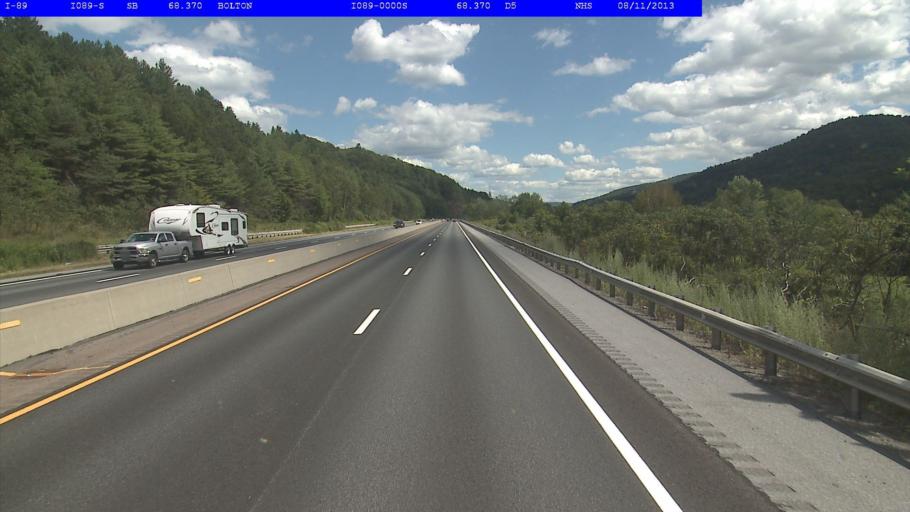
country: US
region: Vermont
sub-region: Washington County
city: Waterbury
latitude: 44.3621
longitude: -72.8371
